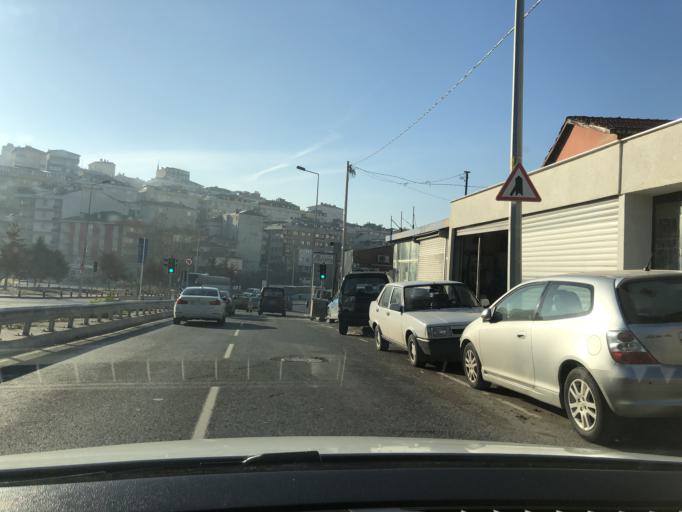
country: TR
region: Istanbul
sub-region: Atasehir
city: Atasehir
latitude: 40.9690
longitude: 29.1223
